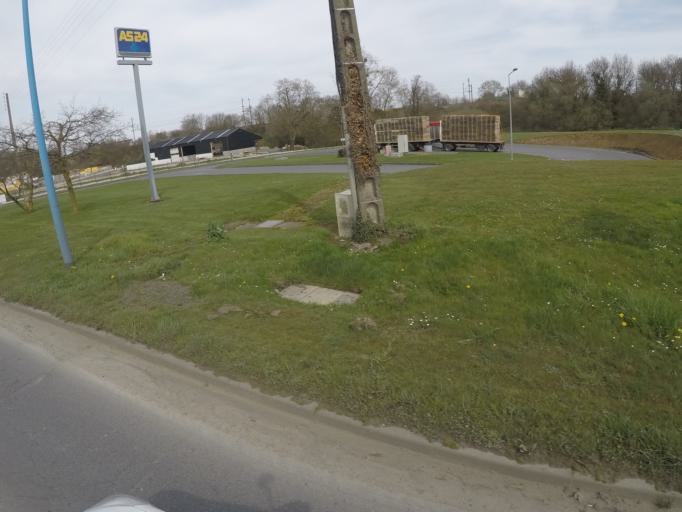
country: FR
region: Brittany
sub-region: Departement des Cotes-d'Armor
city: Plouagat
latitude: 48.5318
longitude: -2.9710
